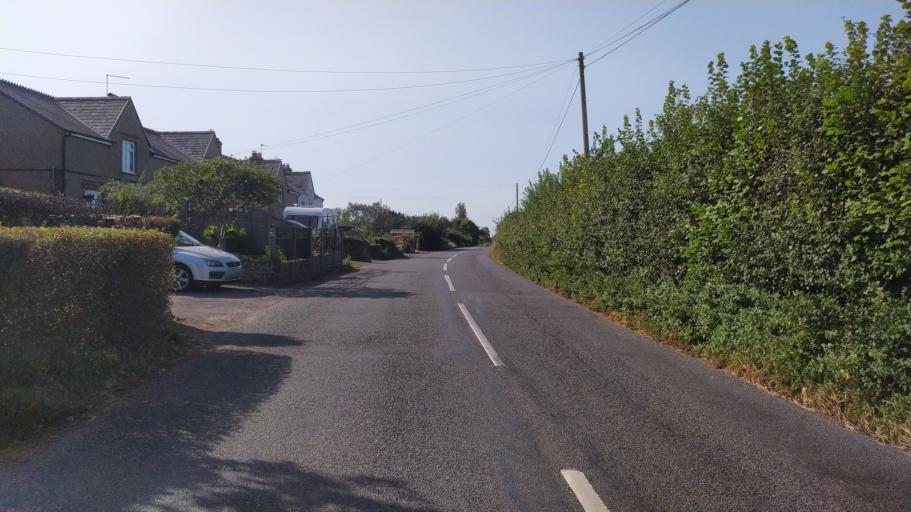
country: GB
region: England
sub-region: Hampshire
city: Havant
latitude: 50.9033
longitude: -0.9609
